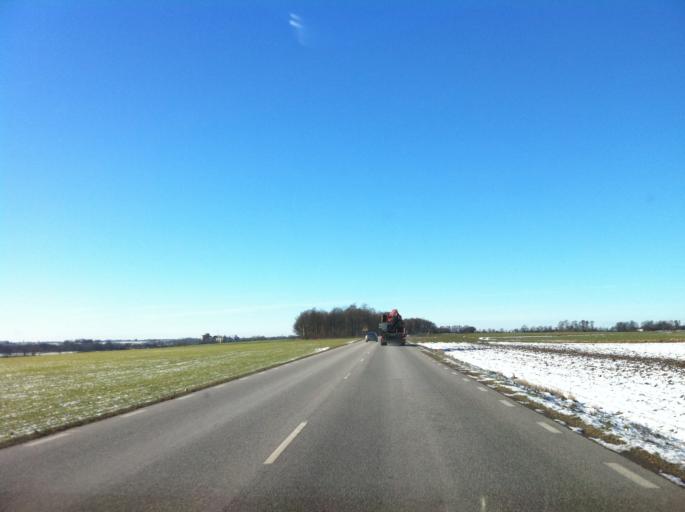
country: SE
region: Skane
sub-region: Lunds Kommun
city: Lund
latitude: 55.7245
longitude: 13.2266
